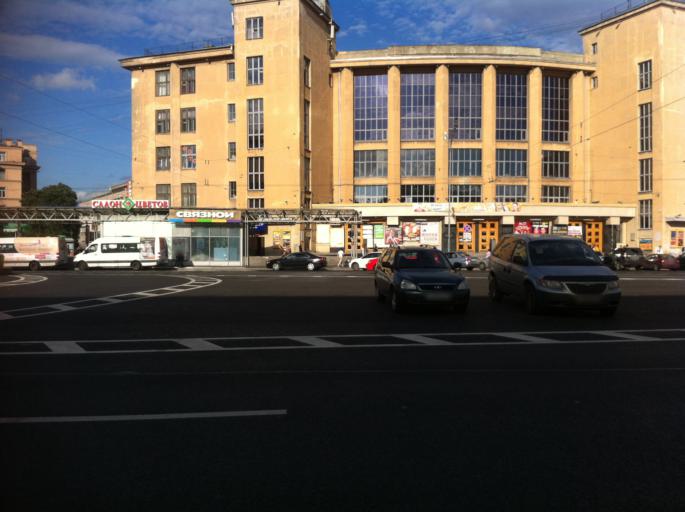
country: RU
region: St.-Petersburg
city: Admiralteisky
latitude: 59.9003
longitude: 30.2741
